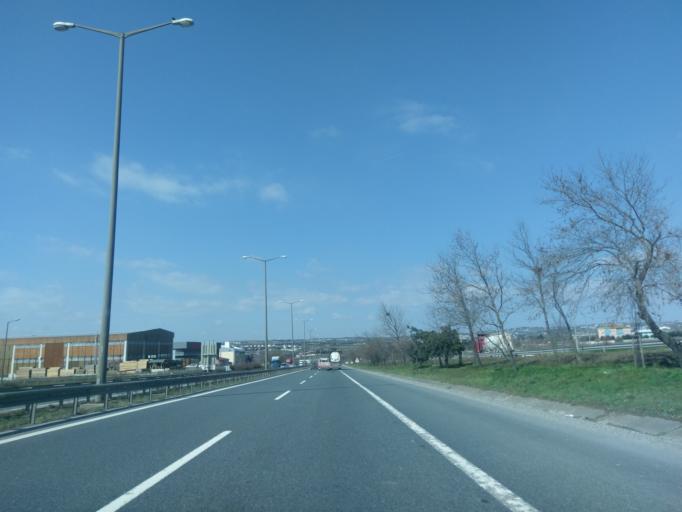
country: TR
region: Istanbul
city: Ortakoy
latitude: 41.0848
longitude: 28.3686
